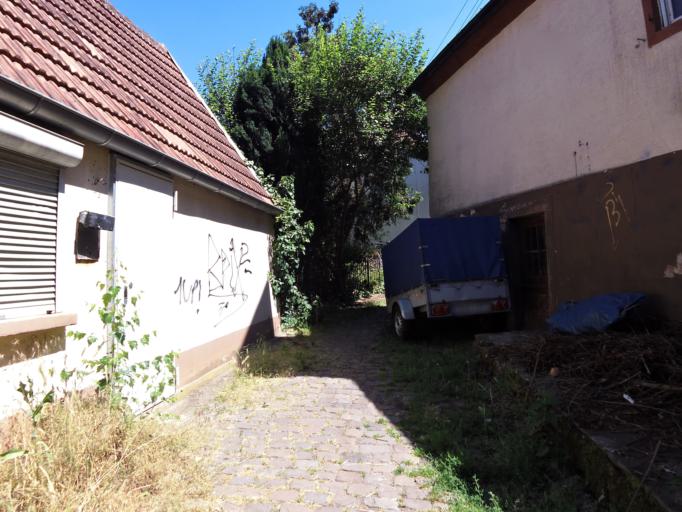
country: DE
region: Rheinland-Pfalz
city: Lambrecht
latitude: 49.3709
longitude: 8.0673
